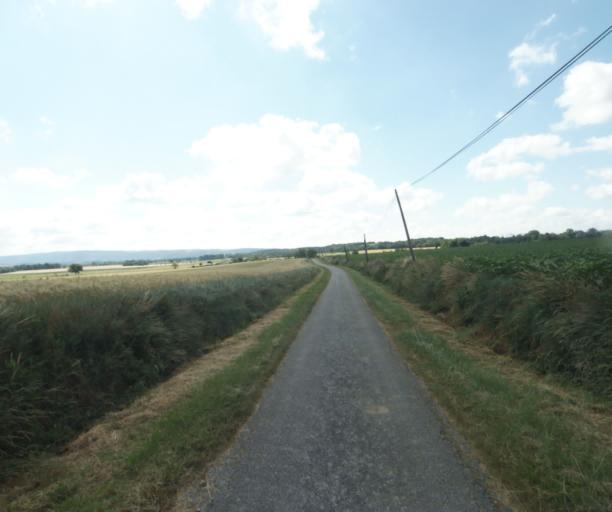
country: FR
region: Midi-Pyrenees
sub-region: Departement de la Haute-Garonne
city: Saint-Felix-Lauragais
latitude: 43.4395
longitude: 1.9134
